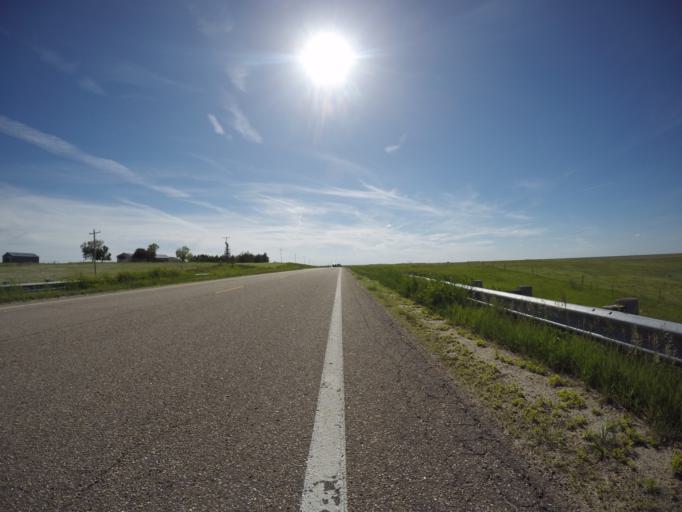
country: US
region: Kansas
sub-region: Cheyenne County
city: Saint Francis
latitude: 39.7566
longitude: -102.0201
